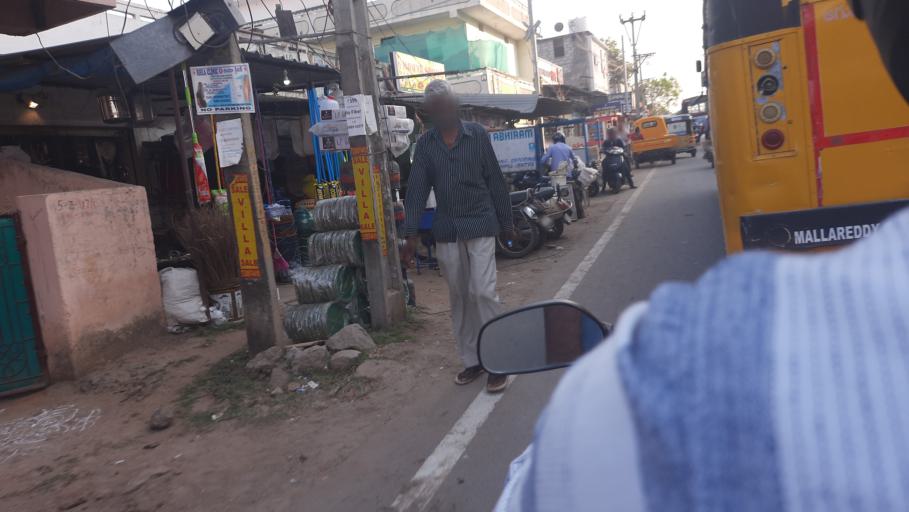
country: IN
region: Telangana
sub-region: Rangareddi
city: Secunderabad
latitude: 17.5026
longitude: 78.5395
